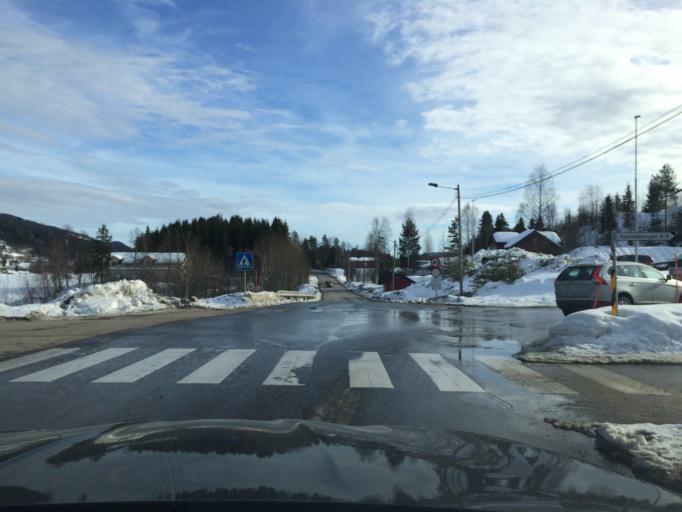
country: NO
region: Hedmark
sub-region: Trysil
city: Innbygda
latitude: 61.3152
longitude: 12.2565
